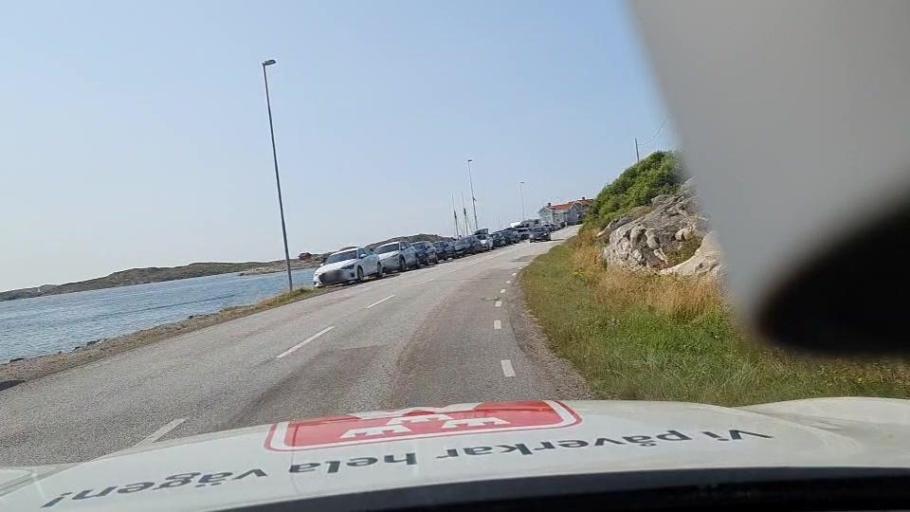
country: SE
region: Vaestra Goetaland
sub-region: Tjorns Kommun
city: Skaerhamn
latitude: 58.1065
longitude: 11.4703
